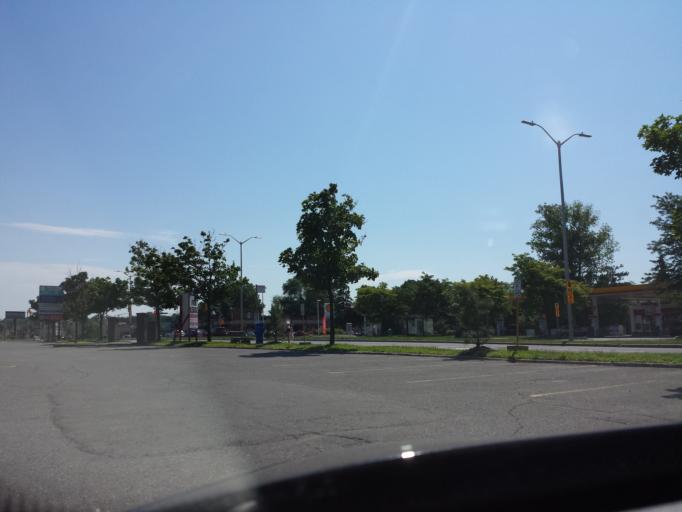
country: CA
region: Ontario
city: Bells Corners
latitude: 45.3688
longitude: -75.7744
